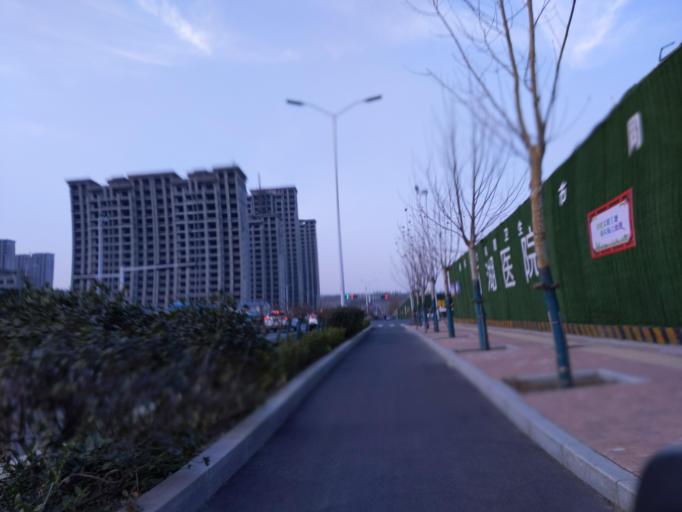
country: CN
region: Henan Sheng
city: Puyang
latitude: 35.8134
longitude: 115.0117
